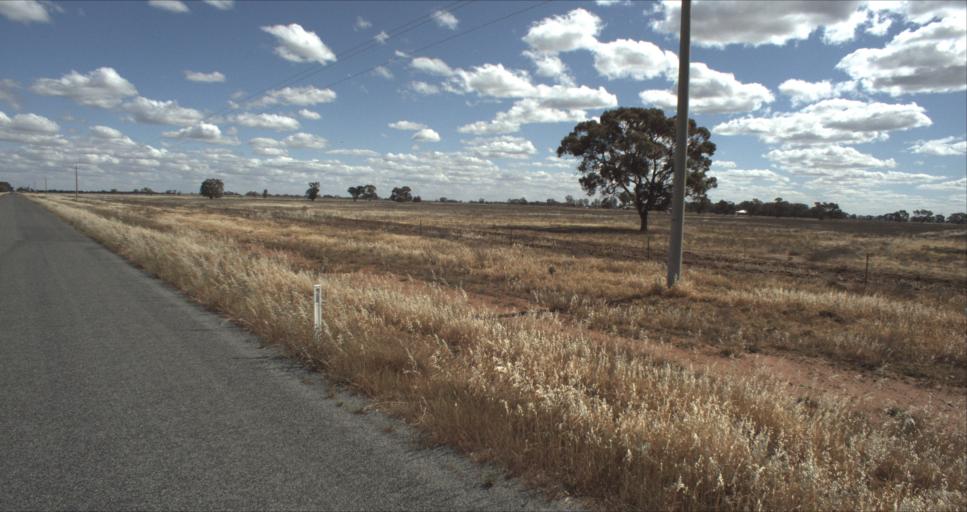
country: AU
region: New South Wales
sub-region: Leeton
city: Leeton
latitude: -34.4623
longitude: 146.2525
